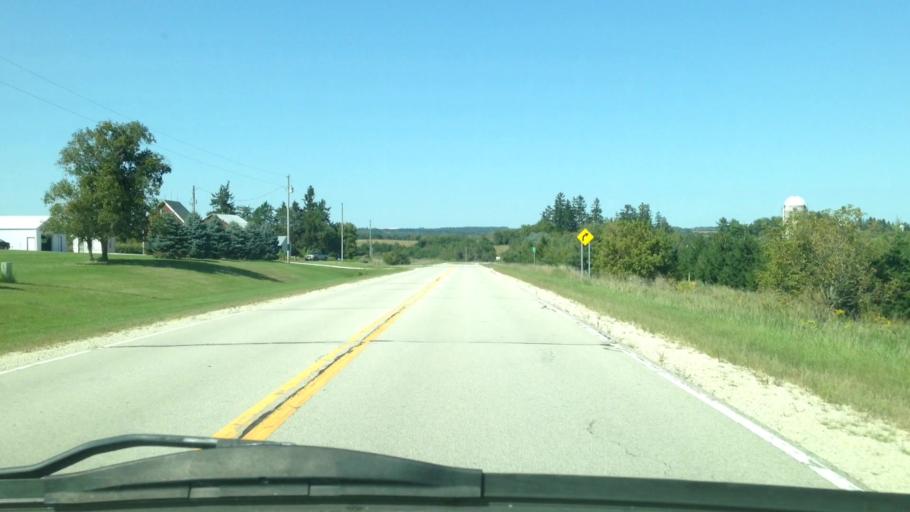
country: US
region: Minnesota
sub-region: Houston County
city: Spring Grove
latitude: 43.6383
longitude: -91.7903
